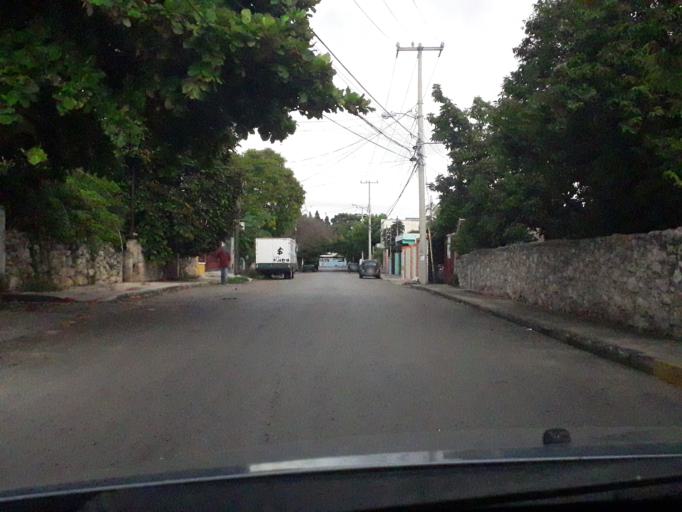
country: MX
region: Yucatan
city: Merida
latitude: 21.0192
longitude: -89.6335
